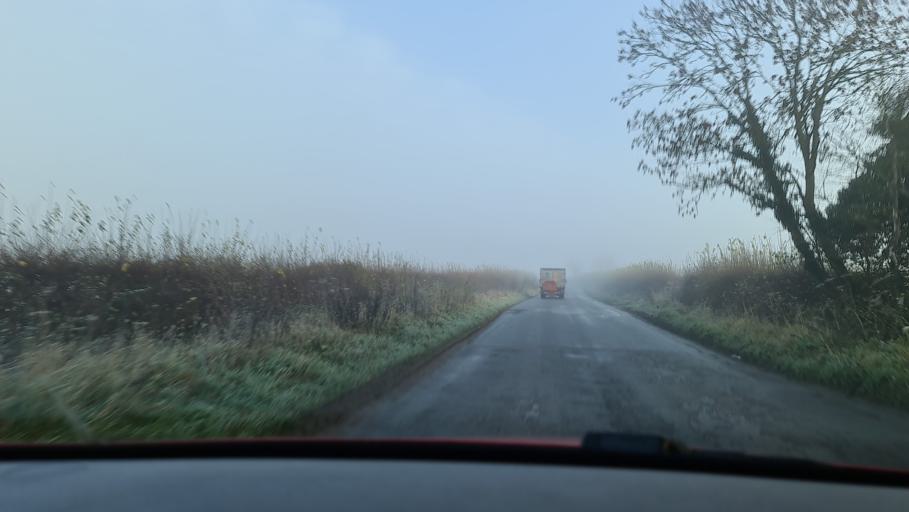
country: GB
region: England
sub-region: Buckinghamshire
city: Aylesbury
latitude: 51.7805
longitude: -0.8053
